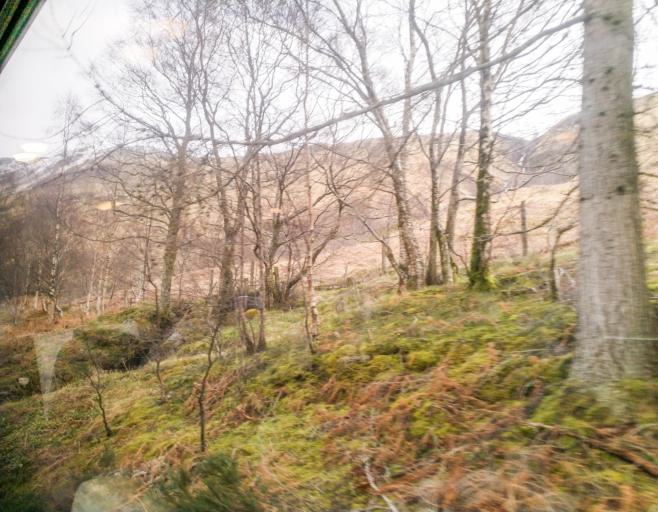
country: GB
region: Scotland
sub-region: Highland
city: Spean Bridge
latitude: 56.8133
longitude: -4.7157
